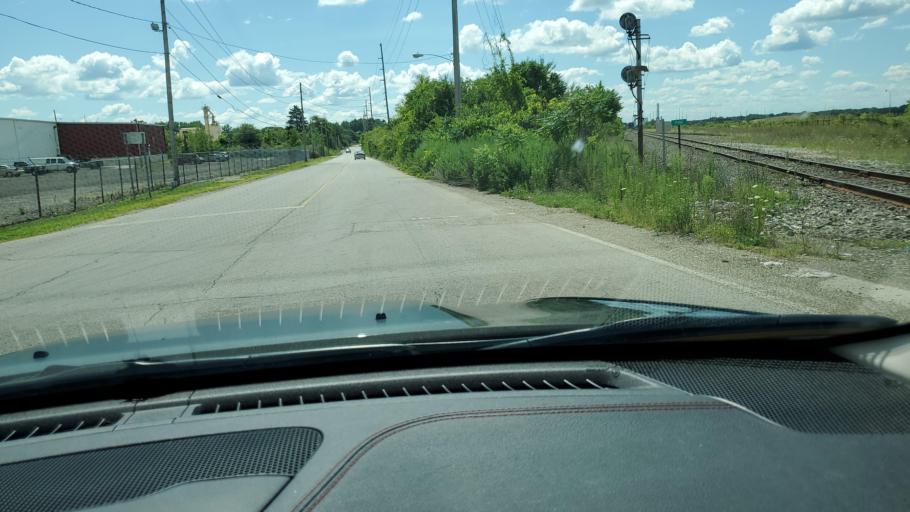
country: US
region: Ohio
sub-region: Trumbull County
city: Warren
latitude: 41.2253
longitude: -80.8104
